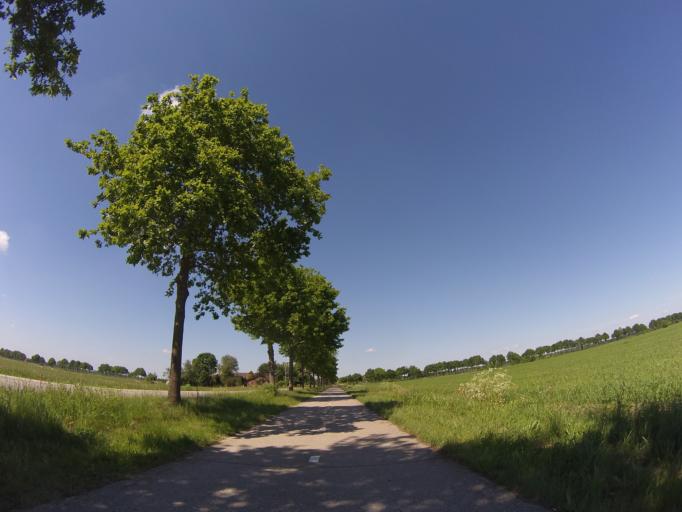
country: NL
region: Drenthe
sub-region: Gemeente Hoogeveen
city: Hoogeveen
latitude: 52.7709
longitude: 6.5880
